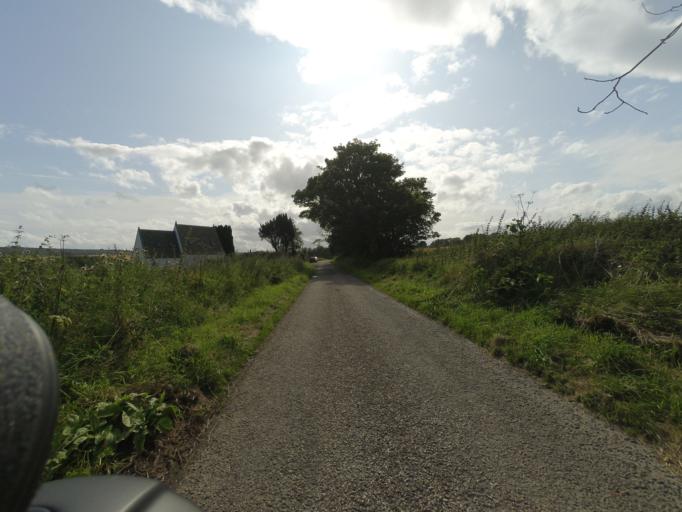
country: GB
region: Scotland
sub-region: Highland
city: Invergordon
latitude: 57.6644
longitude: -4.1705
